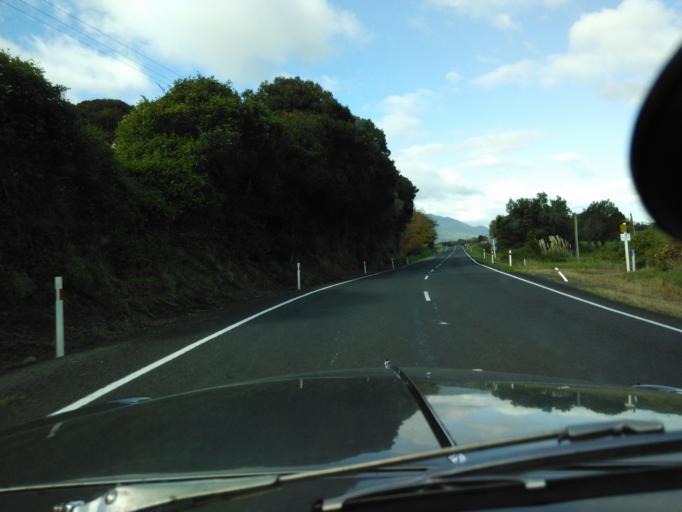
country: NZ
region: Waikato
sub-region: Hauraki District
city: Paeroa
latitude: -37.4533
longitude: 175.6507
